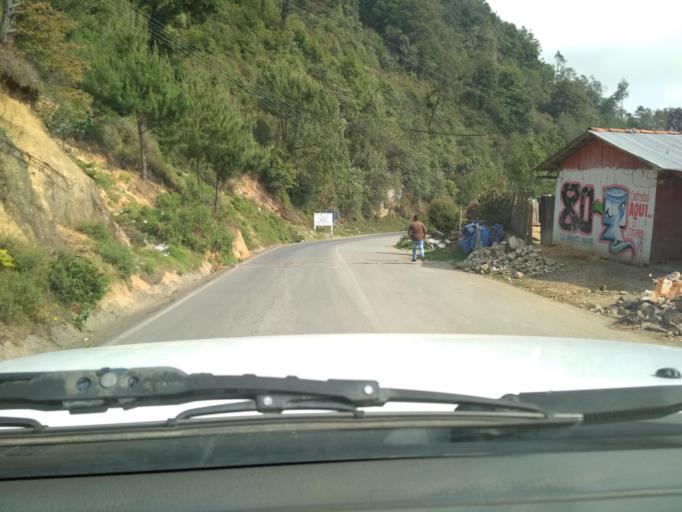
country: MX
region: Veracruz
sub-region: Soledad Atzompa
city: Tlatilpa
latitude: 18.7506
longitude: -97.1541
